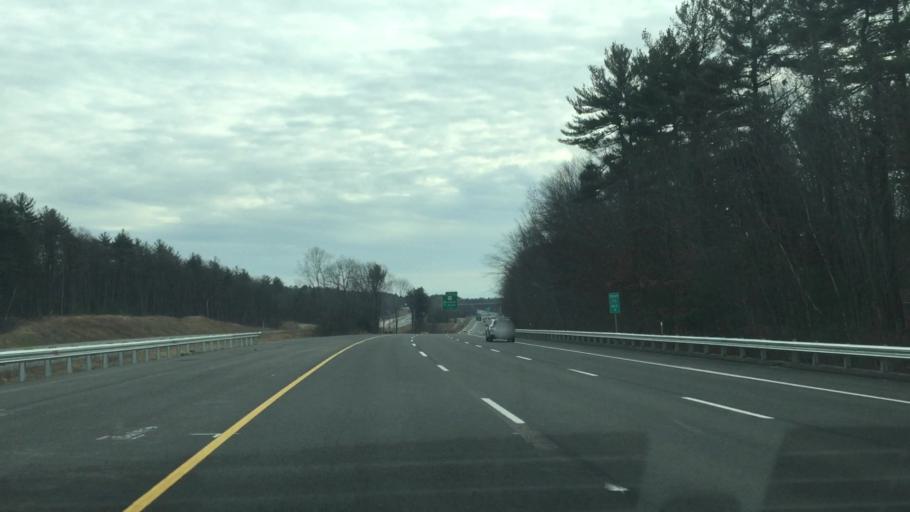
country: US
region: New Hampshire
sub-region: Rockingham County
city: Windham
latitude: 42.8318
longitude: -71.2950
